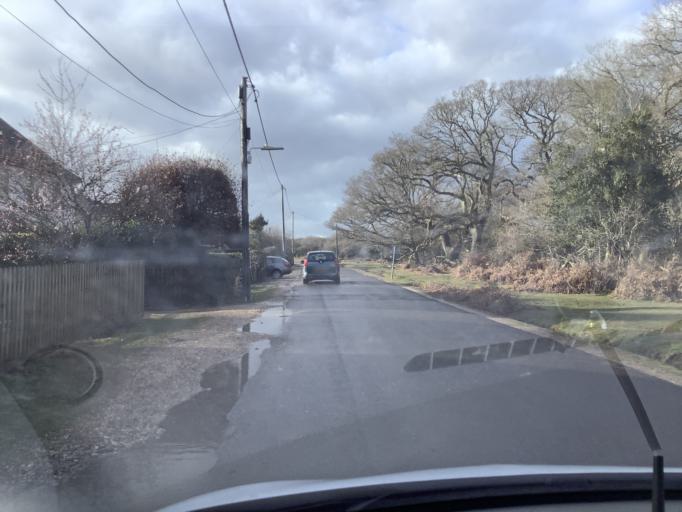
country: GB
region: England
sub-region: Hampshire
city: Brockenhurst
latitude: 50.8263
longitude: -1.5627
